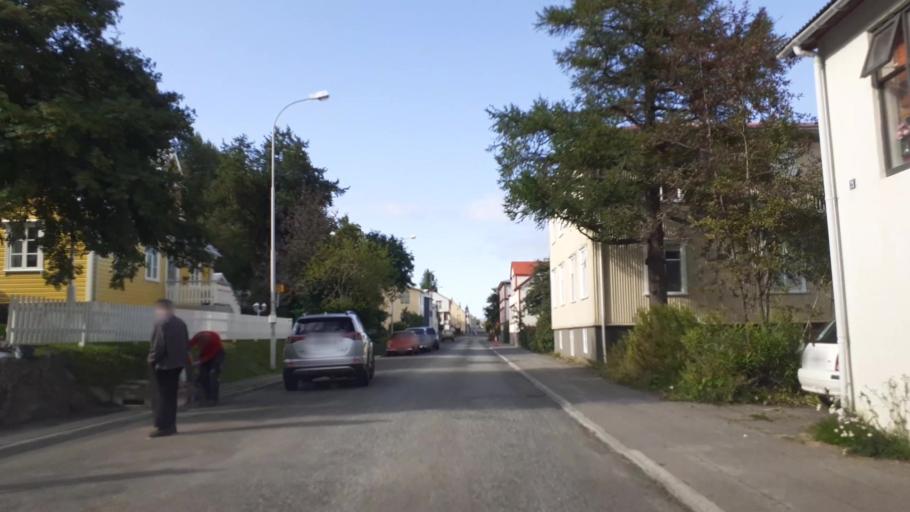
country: IS
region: Northeast
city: Akureyri
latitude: 65.6693
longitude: -18.0861
